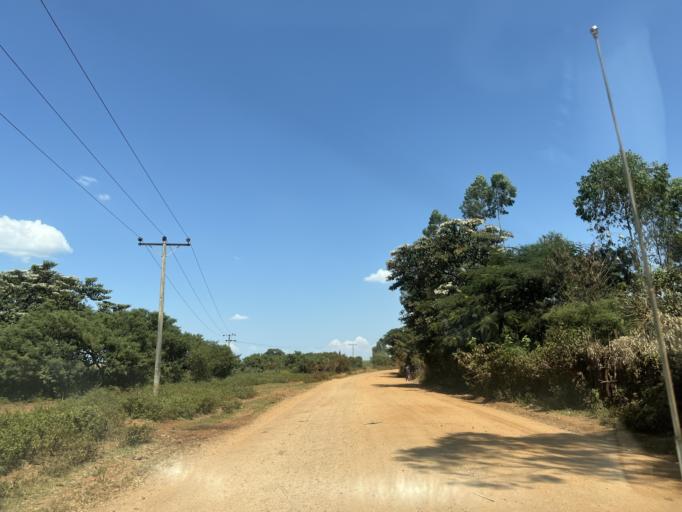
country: ET
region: Oromiya
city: Shambu
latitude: 9.3651
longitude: 36.5134
